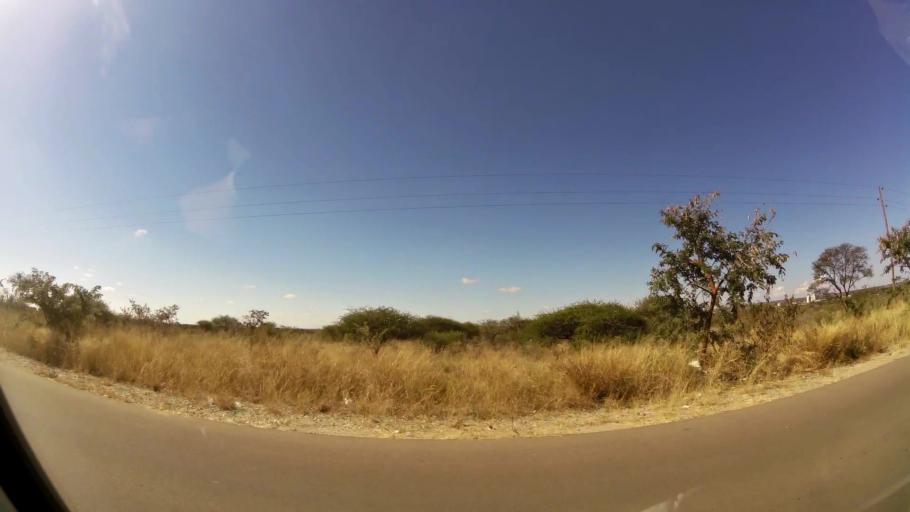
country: ZA
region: Limpopo
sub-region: Capricorn District Municipality
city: Polokwane
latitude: -23.8623
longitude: 29.4273
